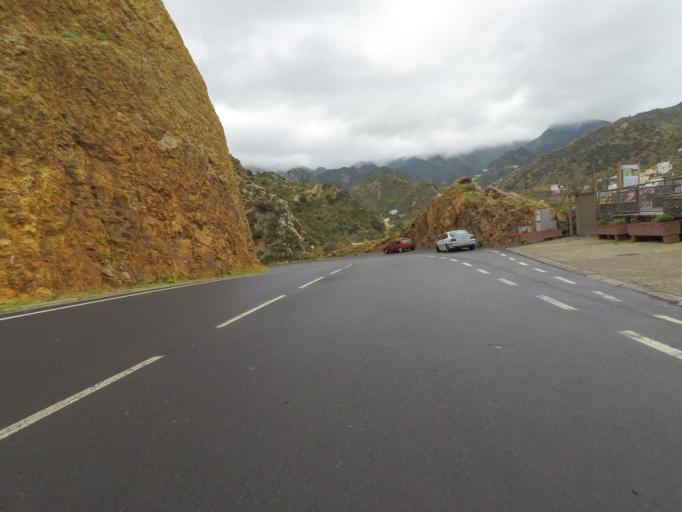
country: ES
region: Canary Islands
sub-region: Provincia de Santa Cruz de Tenerife
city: Vallehermosa
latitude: 28.1828
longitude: -17.2619
